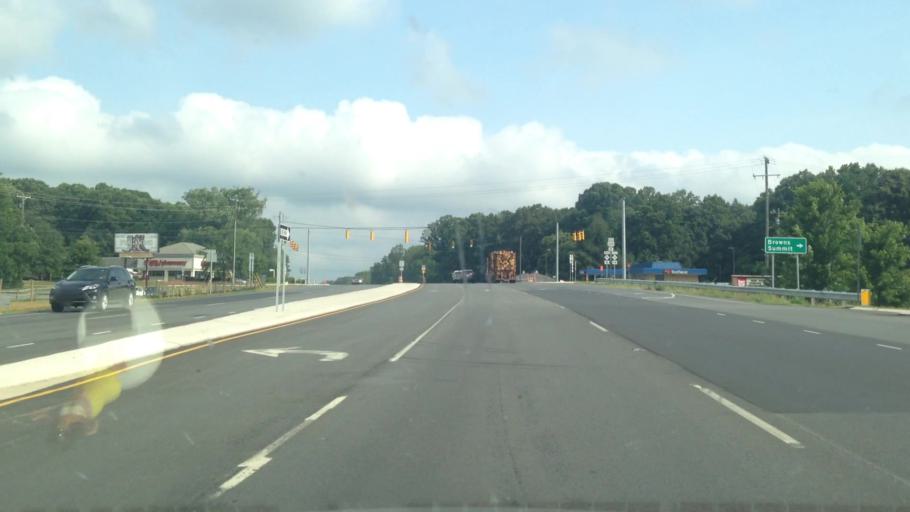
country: US
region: North Carolina
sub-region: Guilford County
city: Summerfield
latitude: 36.1931
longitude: -79.8916
